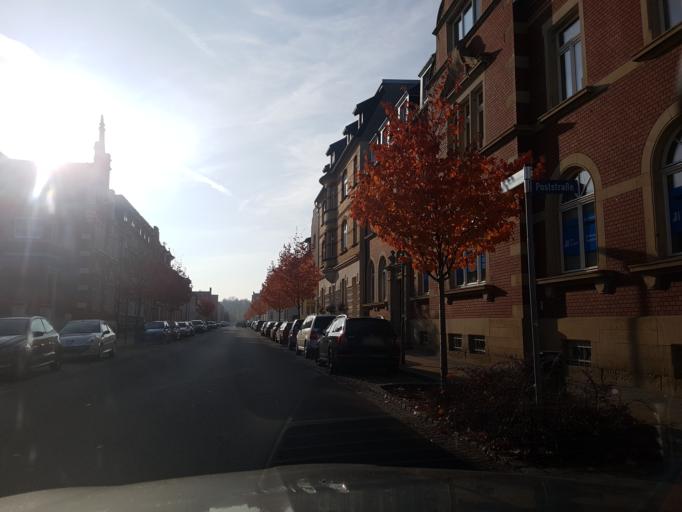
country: DE
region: Brandenburg
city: Elsterwerda
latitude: 51.4587
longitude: 13.5199
